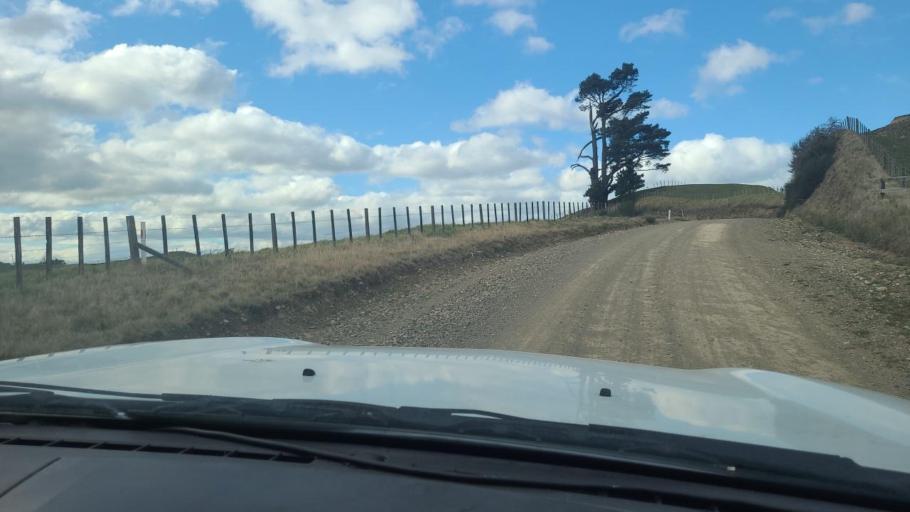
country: NZ
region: Hawke's Bay
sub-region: Hastings District
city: Hastings
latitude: -39.6868
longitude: 176.4685
